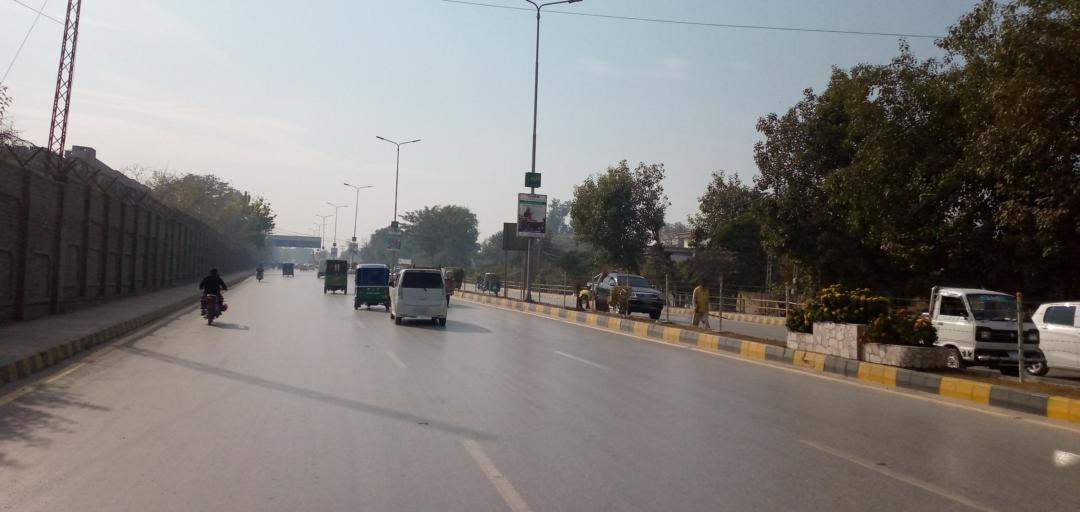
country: PK
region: Khyber Pakhtunkhwa
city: Peshawar
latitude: 34.0093
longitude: 71.5382
